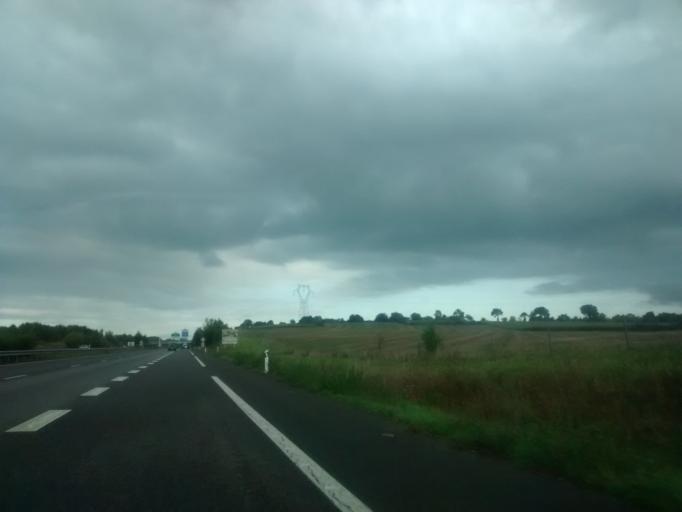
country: FR
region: Brittany
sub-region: Departement d'Ille-et-Vilaine
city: Fouillard
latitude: 48.1424
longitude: -1.5860
